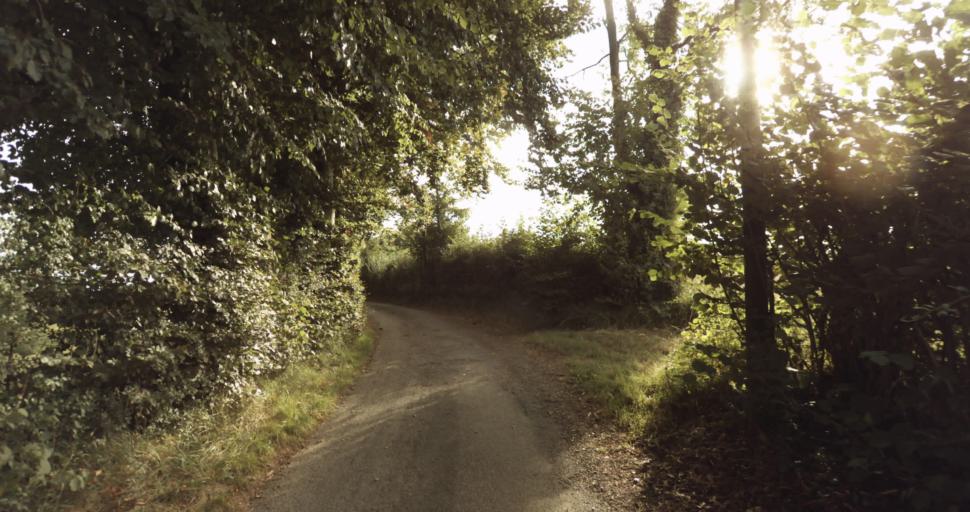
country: FR
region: Lower Normandy
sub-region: Departement de l'Orne
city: Vimoutiers
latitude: 48.8608
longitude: 0.2452
